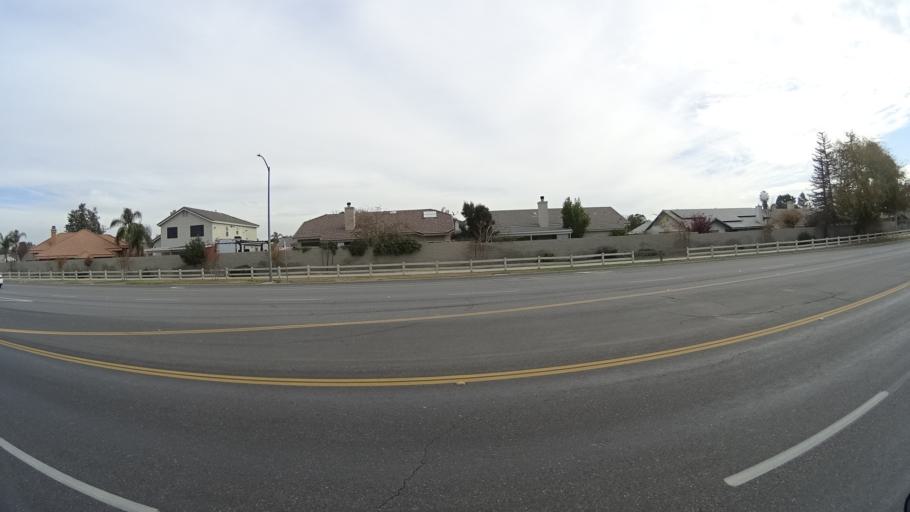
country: US
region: California
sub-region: Kern County
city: Rosedale
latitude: 35.4043
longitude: -119.1277
